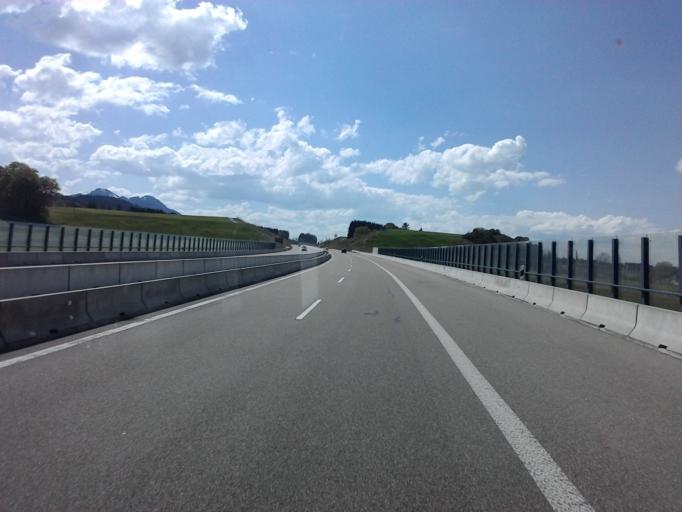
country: DE
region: Bavaria
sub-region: Swabia
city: Eisenberg
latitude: 47.6298
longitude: 10.5972
